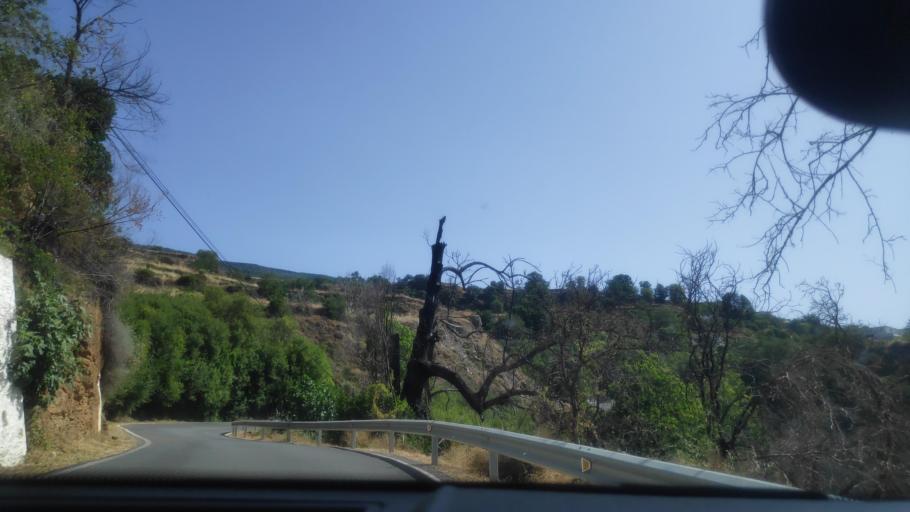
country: ES
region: Andalusia
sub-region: Provincia de Granada
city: Portugos
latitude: 36.9394
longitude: -3.3222
